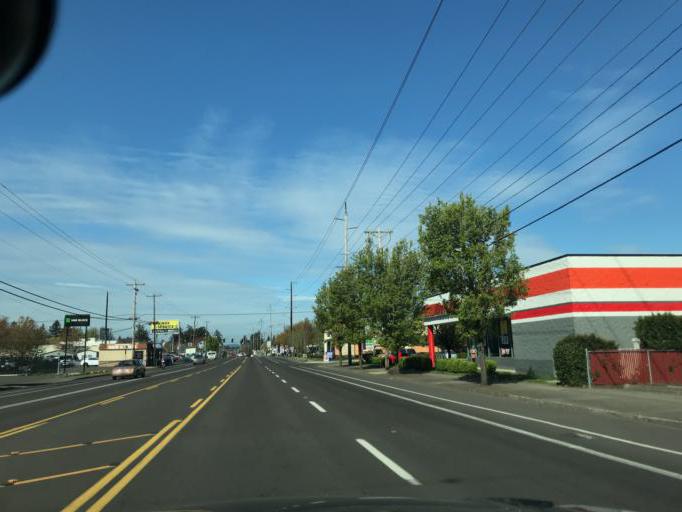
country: US
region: Oregon
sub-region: Multnomah County
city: Gresham
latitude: 45.5046
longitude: -122.4939
